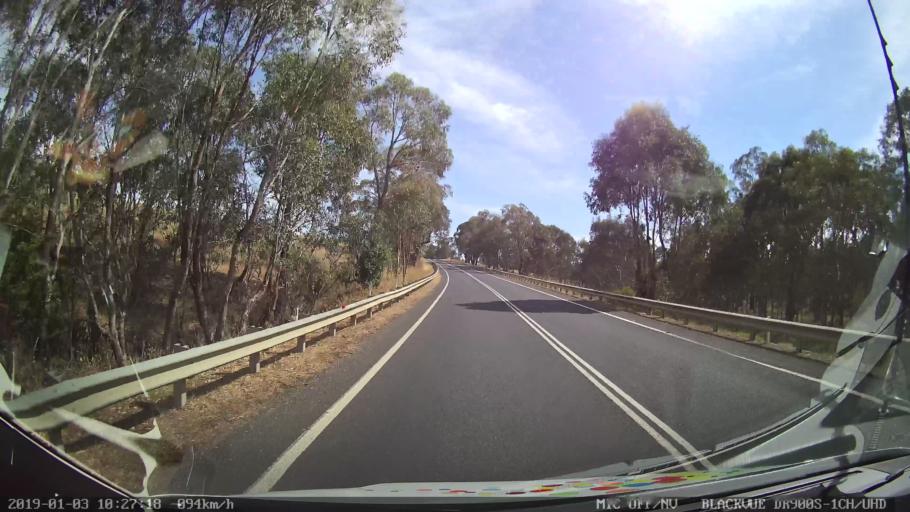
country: AU
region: New South Wales
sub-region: Young
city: Young
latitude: -34.4037
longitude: 148.2583
